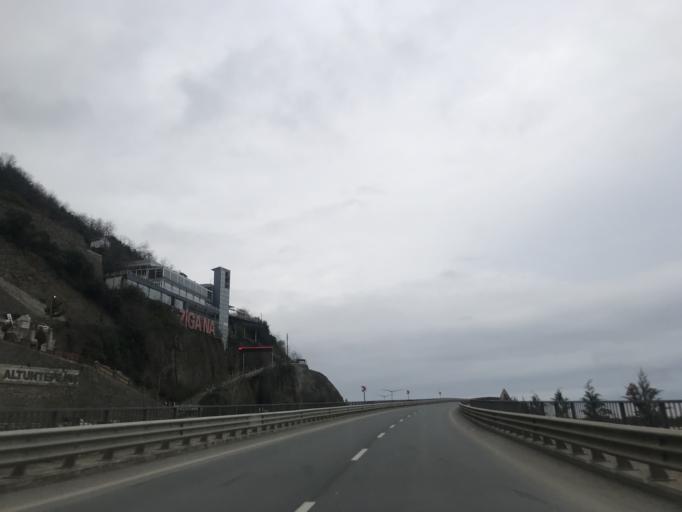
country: TR
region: Trabzon
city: Akcaabat
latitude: 41.0006
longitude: 39.6375
